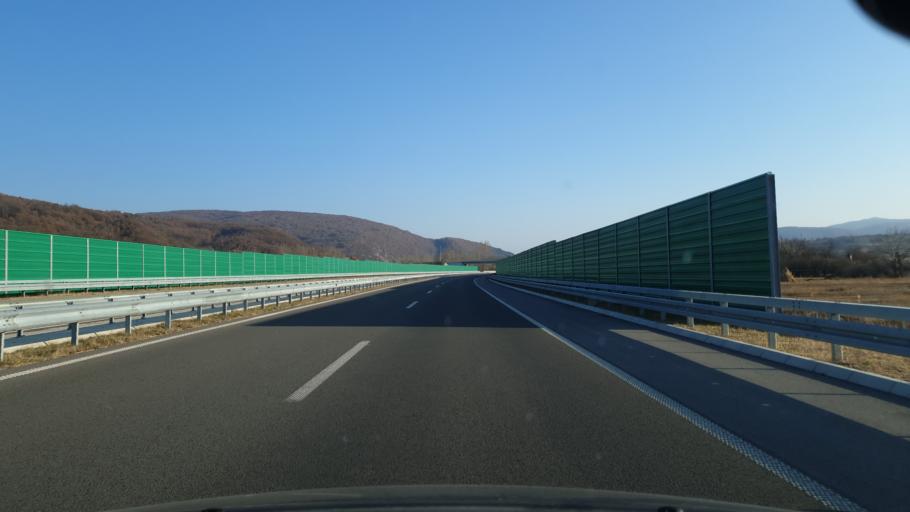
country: RS
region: Central Serbia
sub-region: Pirotski Okrug
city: Dimitrovgrad
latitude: 43.0480
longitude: 22.7035
